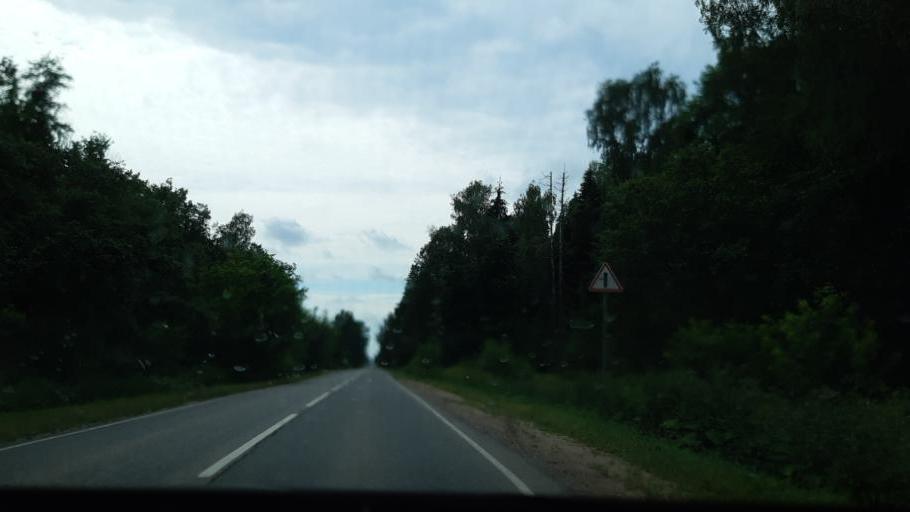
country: RU
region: Moskovskaya
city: Vereya
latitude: 55.3806
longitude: 36.2858
